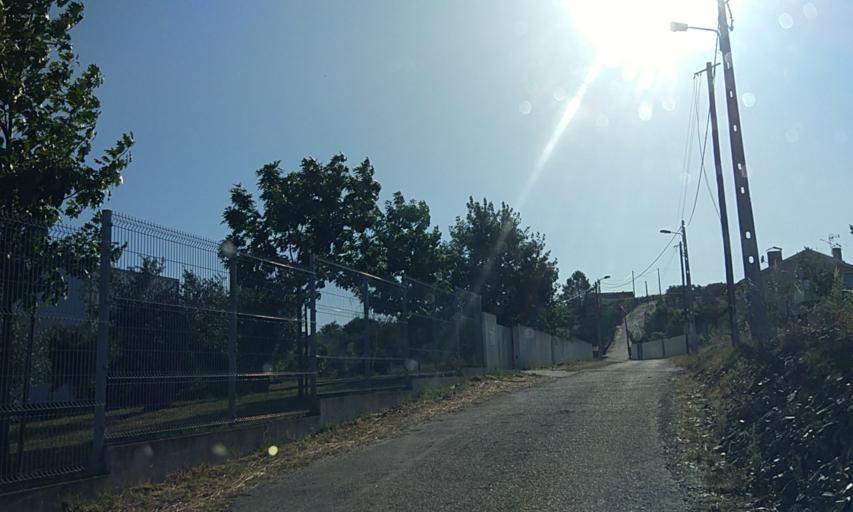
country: PT
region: Viseu
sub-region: Sao Joao da Pesqueira
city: Sao Joao da Pesqueira
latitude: 41.1530
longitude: -7.4203
